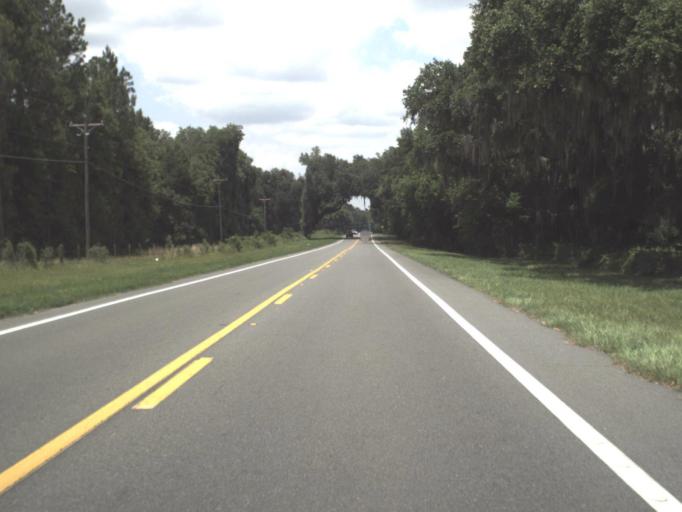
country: US
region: Florida
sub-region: Alachua County
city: Gainesville
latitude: 29.5887
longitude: -82.3896
